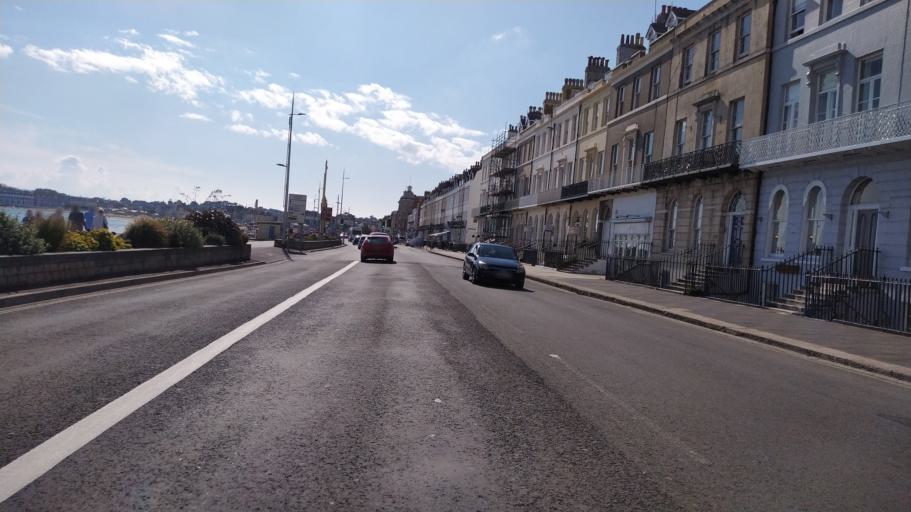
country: GB
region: England
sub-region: Dorset
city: Weymouth
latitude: 50.6162
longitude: -2.4519
